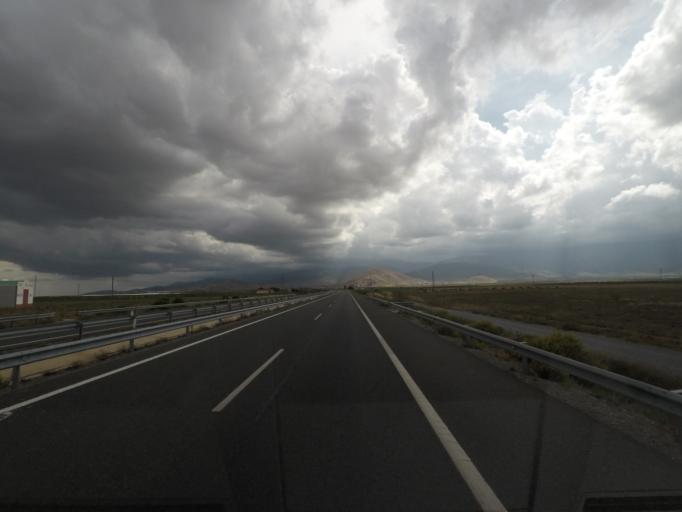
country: ES
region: Andalusia
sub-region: Provincia de Granada
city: Alquife
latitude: 37.2183
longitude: -3.0749
